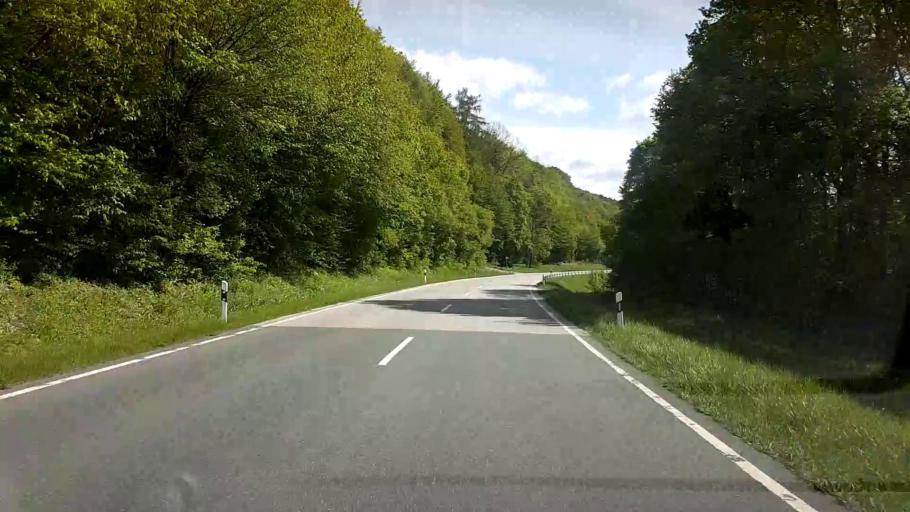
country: DE
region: Bavaria
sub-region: Upper Franconia
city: Ebermannstadt
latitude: 49.7961
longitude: 11.1758
